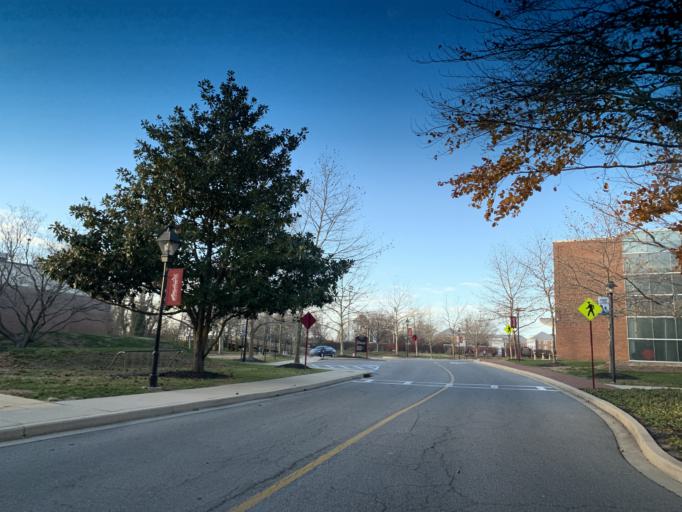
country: US
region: Maryland
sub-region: Kent County
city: Chestertown
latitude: 39.2169
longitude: -76.0700
